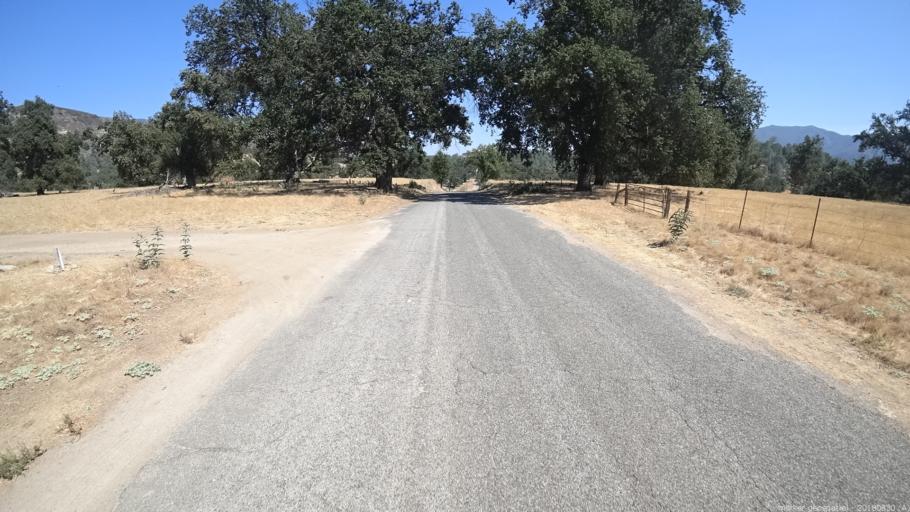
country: US
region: California
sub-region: Monterey County
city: Greenfield
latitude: 36.0833
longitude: -121.3974
